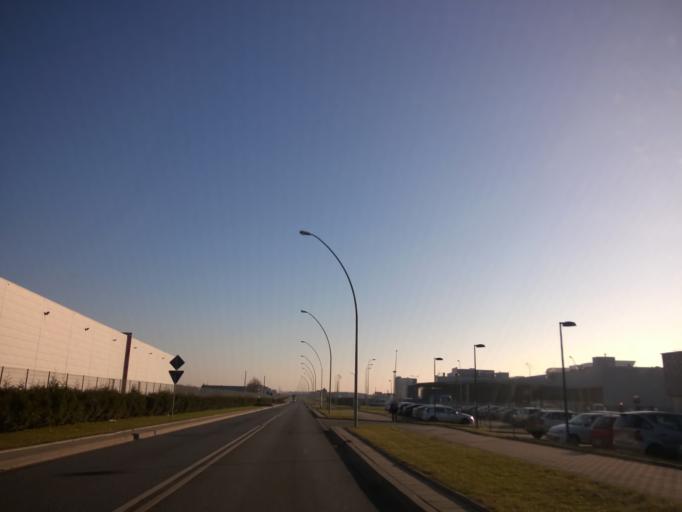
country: PL
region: Lower Silesian Voivodeship
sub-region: Powiat wroclawski
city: Bielany Wroclawskie
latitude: 51.0766
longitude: 16.9528
